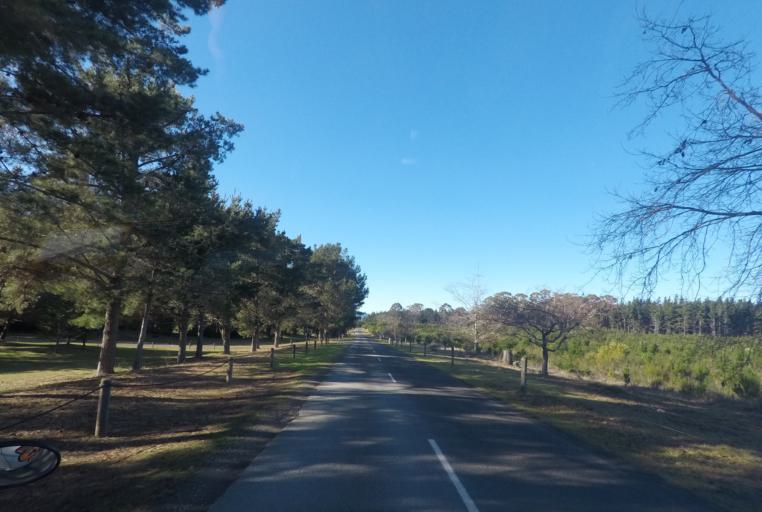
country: NZ
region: Tasman
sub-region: Tasman District
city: Mapua
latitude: -41.2660
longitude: 173.1463
